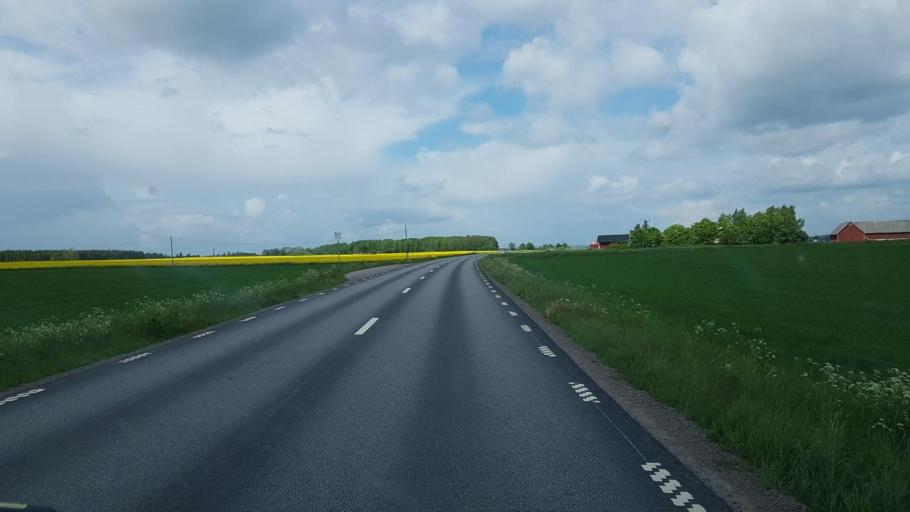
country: SE
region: OEstergoetland
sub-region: Motala Kommun
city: Borensberg
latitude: 58.4866
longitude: 15.2119
